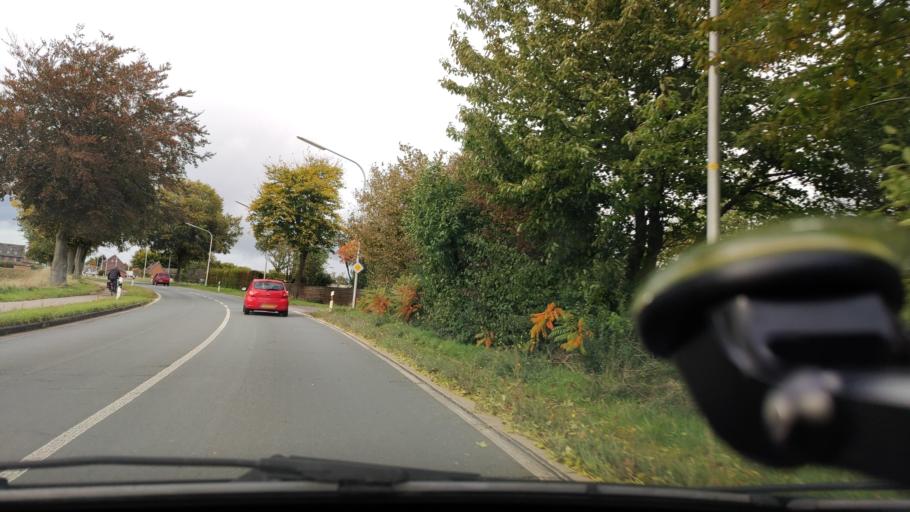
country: NL
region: Limburg
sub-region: Gemeente Roerdalen
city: Vlodrop
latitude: 51.1112
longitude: 6.0618
